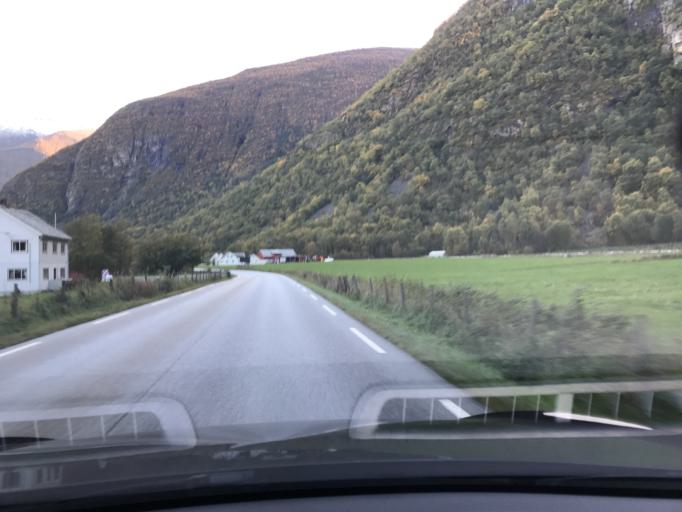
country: NO
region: Sogn og Fjordane
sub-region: Laerdal
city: Laerdalsoyri
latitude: 61.0707
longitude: 7.5005
